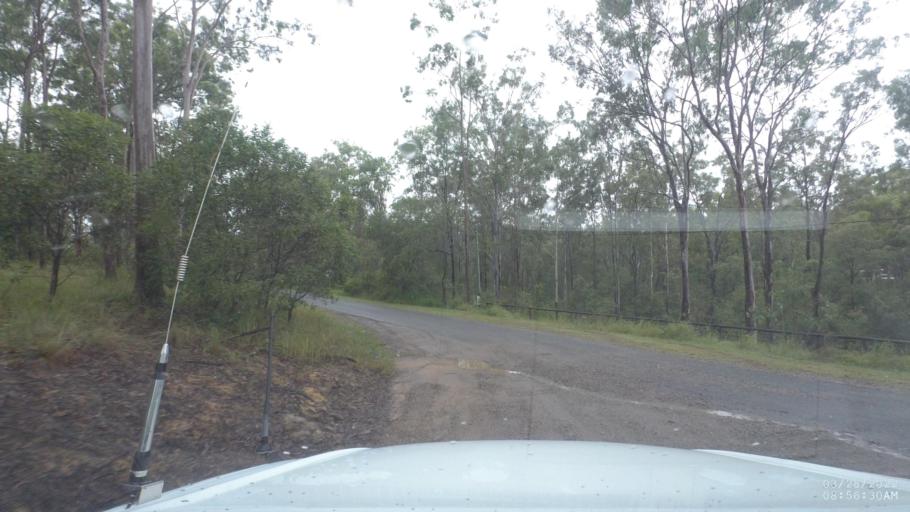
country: AU
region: Queensland
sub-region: Logan
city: Cedar Vale
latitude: -27.8393
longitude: 153.0642
